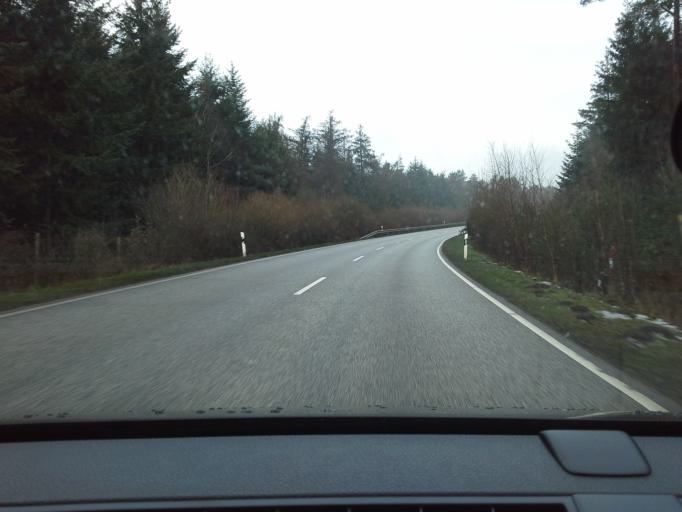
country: DE
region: Schleswig-Holstein
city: Henstedt-Ulzburg
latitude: 53.7447
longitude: 9.9835
